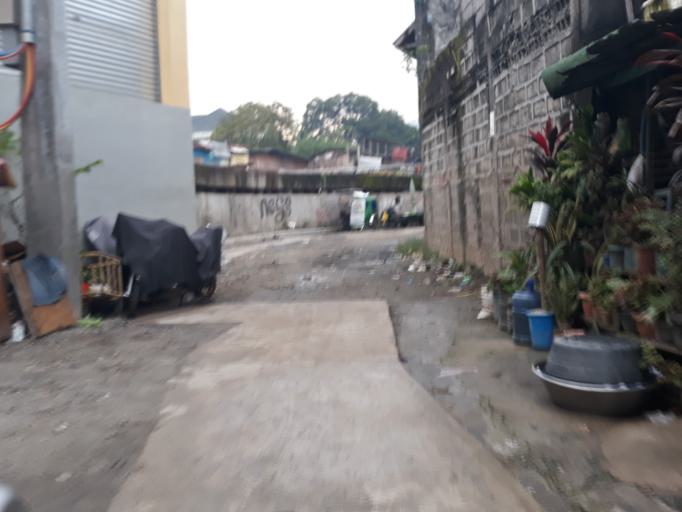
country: PH
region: Metro Manila
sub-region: San Juan
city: San Juan
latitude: 14.6122
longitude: 121.0256
